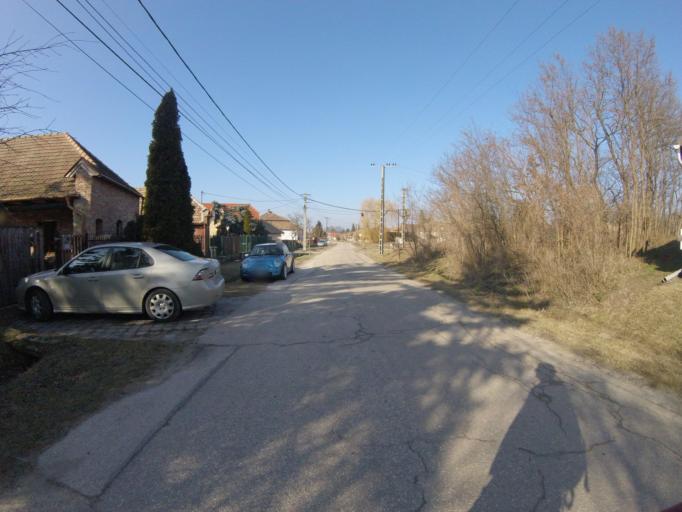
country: HU
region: Komarom-Esztergom
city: Oroszlany
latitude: 47.4818
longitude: 18.3285
